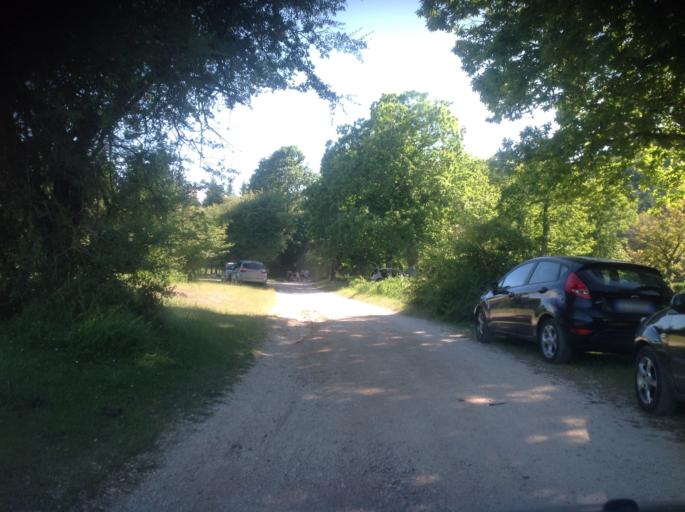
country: IT
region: Latium
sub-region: Provincia di Rieti
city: Limiti di Greccio
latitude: 42.4762
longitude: 12.7091
